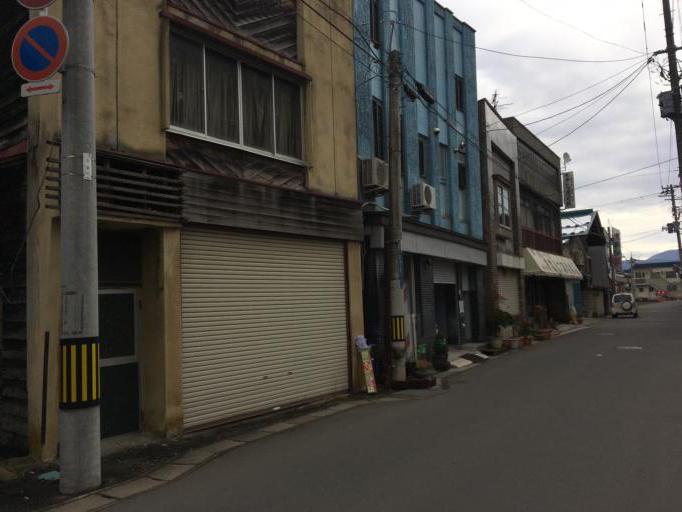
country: JP
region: Aomori
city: Hirosaki
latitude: 40.5197
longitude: 140.5717
